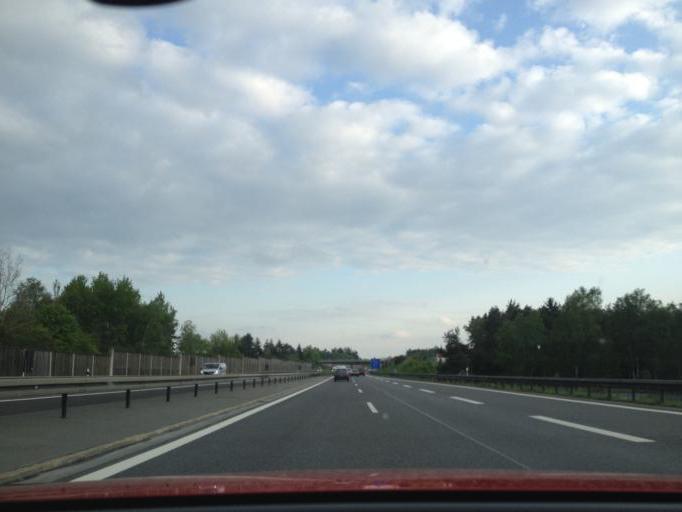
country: DE
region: Bavaria
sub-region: Upper Palatinate
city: Weiden
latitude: 49.6982
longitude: 12.1345
